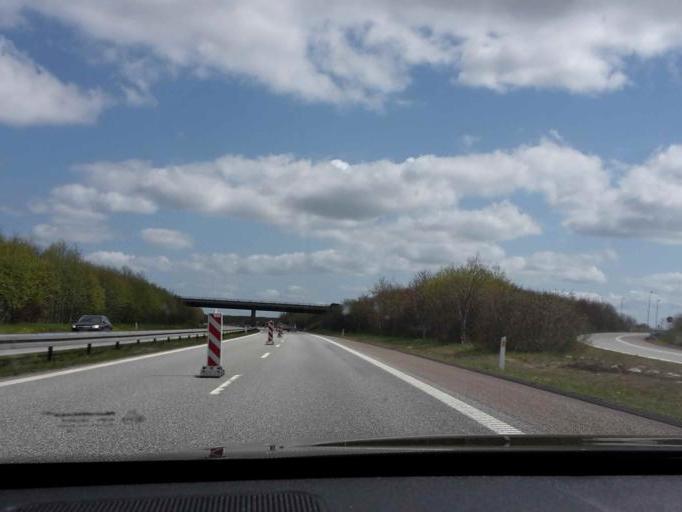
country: DK
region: South Denmark
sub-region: Vejen Kommune
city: Holsted
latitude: 55.5125
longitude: 8.8069
